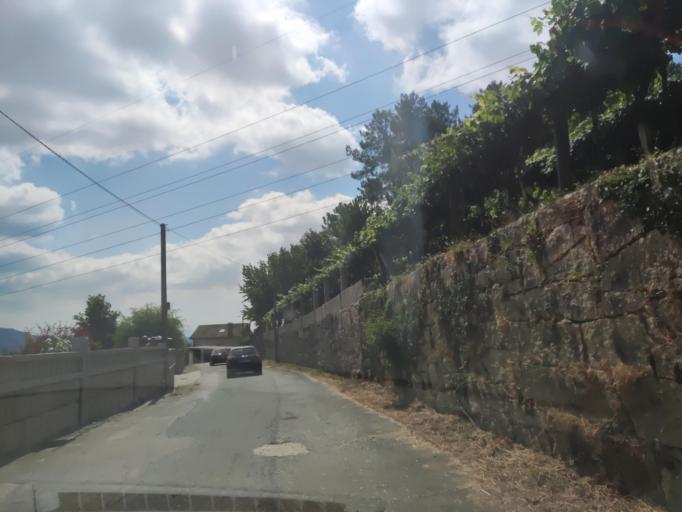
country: ES
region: Galicia
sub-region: Provincia de Pontevedra
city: Porrino
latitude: 42.1538
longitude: -8.6510
